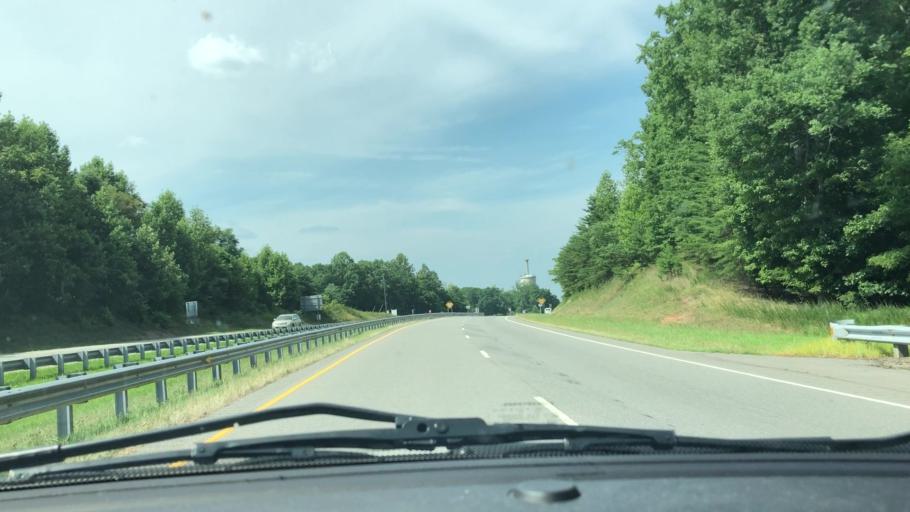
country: US
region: North Carolina
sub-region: Rockingham County
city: Stoneville
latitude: 36.5385
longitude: -79.9130
